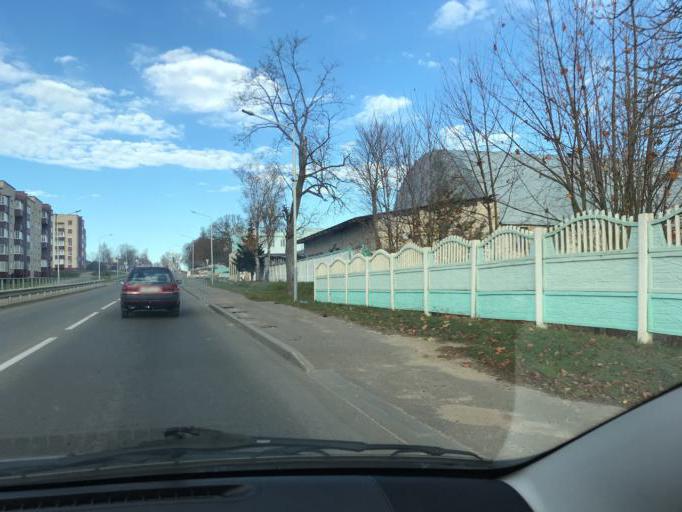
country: BY
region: Vitebsk
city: Haradok
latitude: 55.4684
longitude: 29.9745
